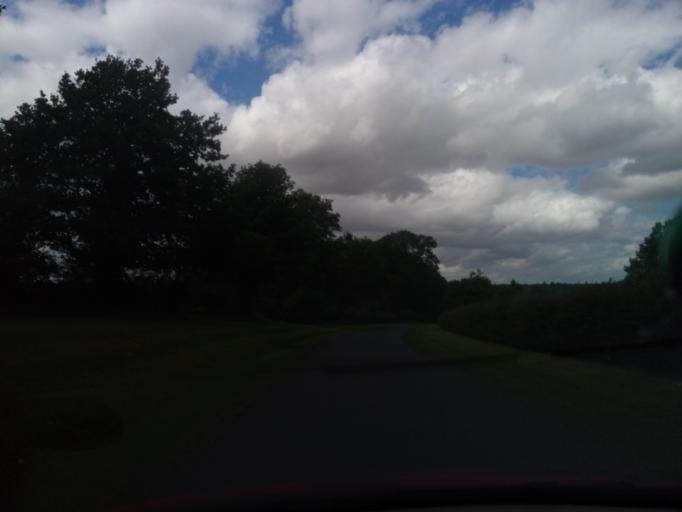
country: GB
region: Scotland
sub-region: The Scottish Borders
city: Coldstream
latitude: 55.6524
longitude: -2.2728
